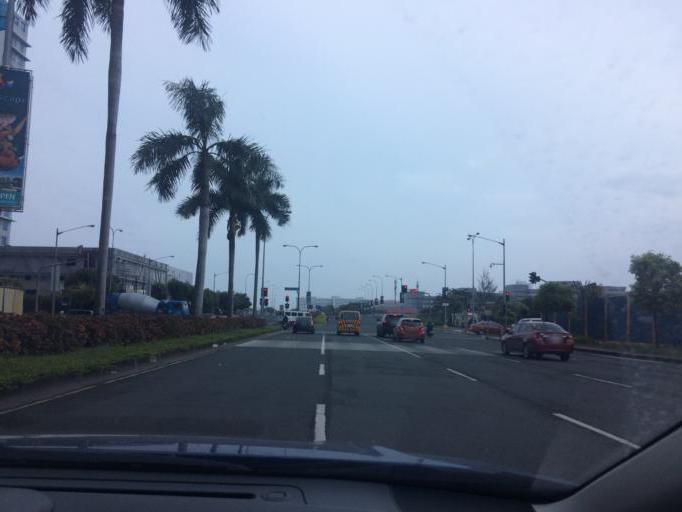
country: PH
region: Metro Manila
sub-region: City of Manila
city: Port Area
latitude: 14.5414
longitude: 120.9833
